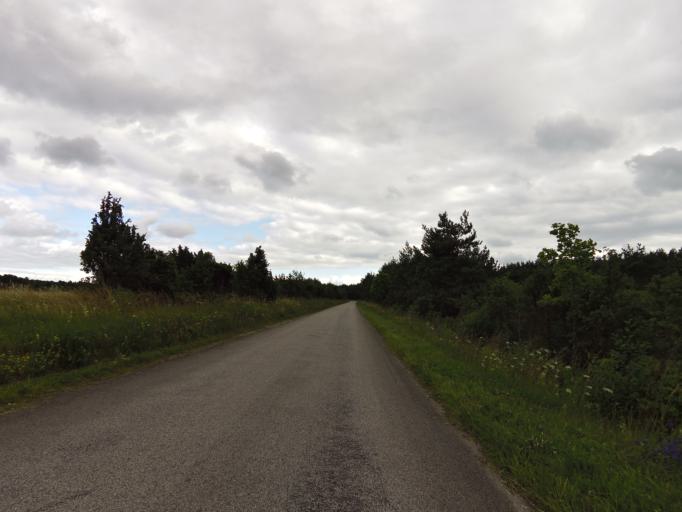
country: EE
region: Laeaene
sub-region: Vormsi vald
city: Hullo
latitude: 58.9841
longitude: 23.2485
